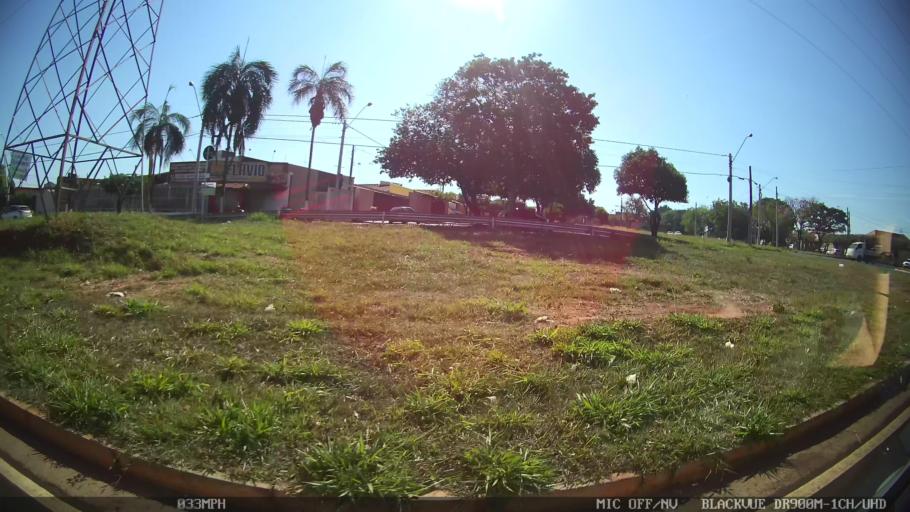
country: BR
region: Sao Paulo
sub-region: Sao Jose Do Rio Preto
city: Sao Jose do Rio Preto
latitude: -20.7637
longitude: -49.3634
